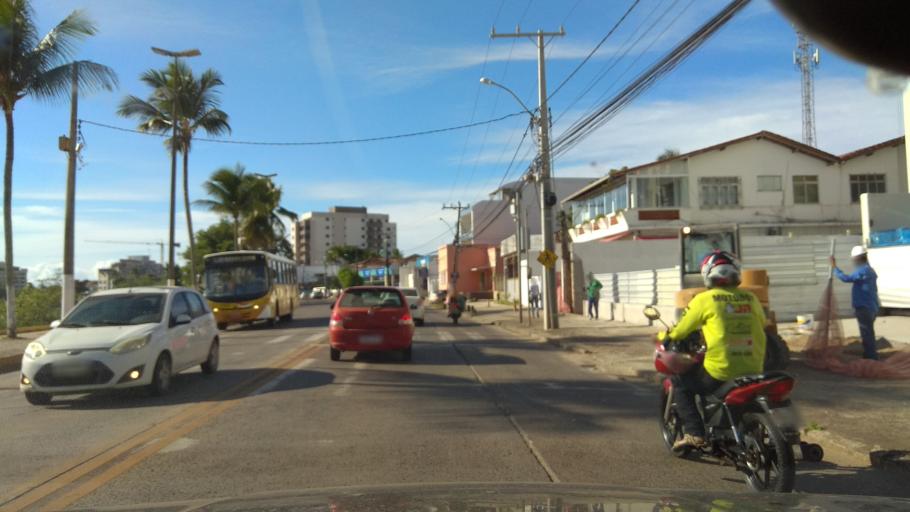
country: BR
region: Bahia
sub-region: Ilheus
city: Ilheus
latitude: -14.8106
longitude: -39.0342
